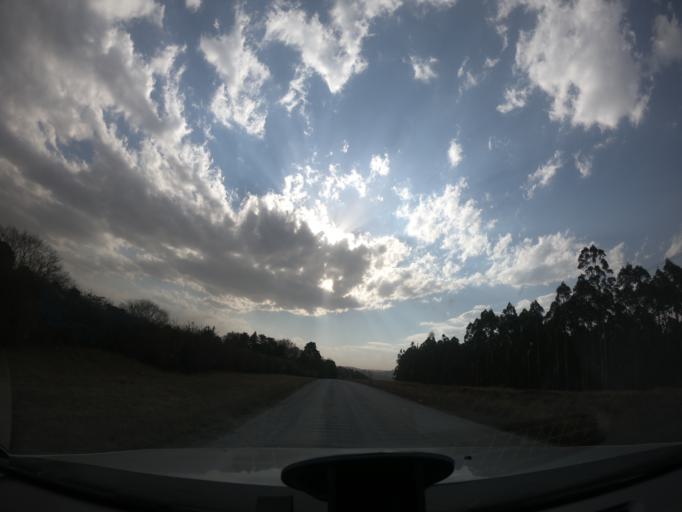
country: ZA
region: KwaZulu-Natal
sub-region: uMgungundlovu District Municipality
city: Howick
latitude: -29.4264
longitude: 30.1067
